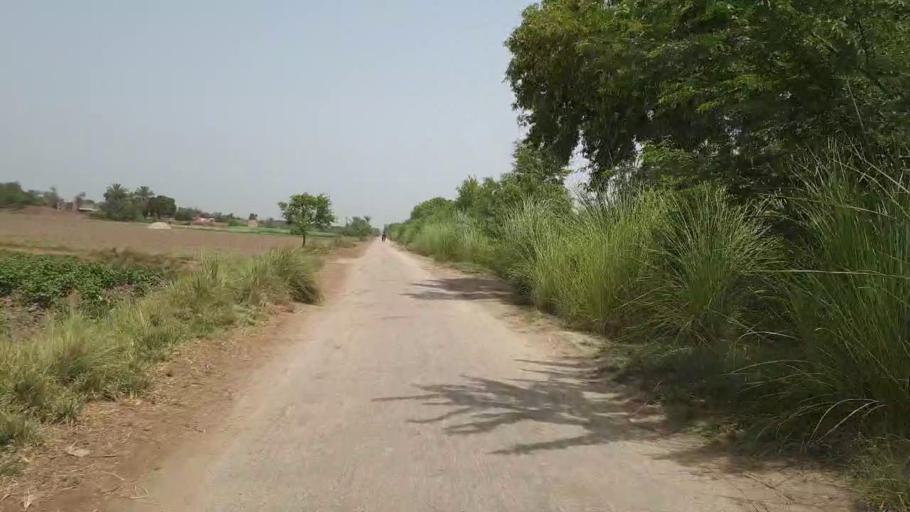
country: PK
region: Sindh
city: Nawabshah
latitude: 26.2994
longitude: 68.3054
